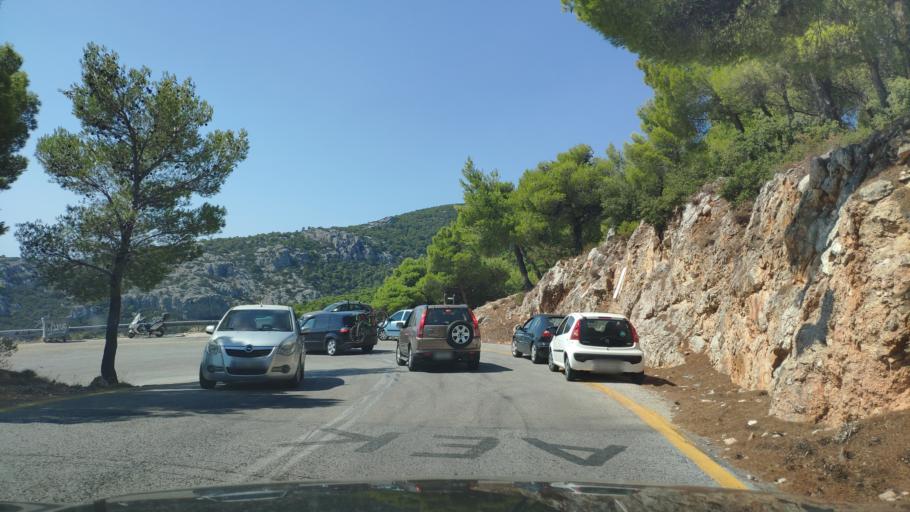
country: GR
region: Attica
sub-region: Nomarchia Anatolikis Attikis
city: Thrakomakedones
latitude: 38.1359
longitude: 23.7288
